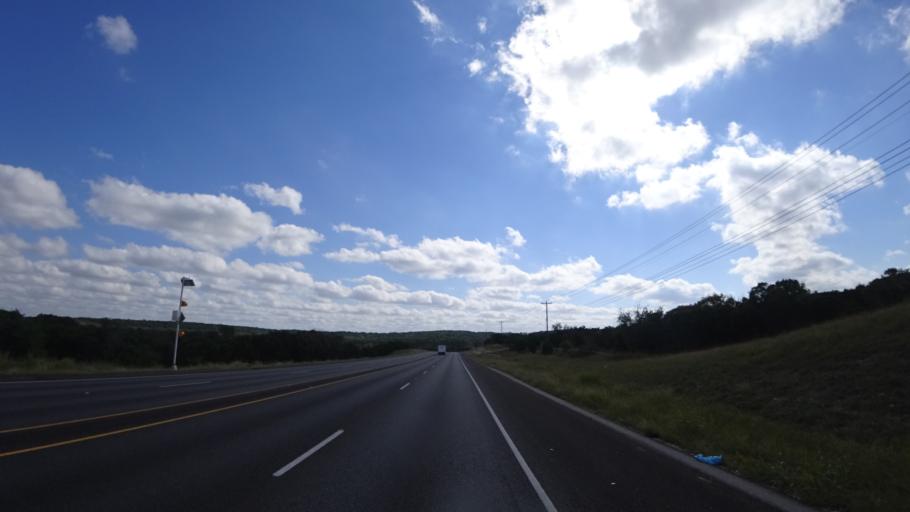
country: US
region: Texas
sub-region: Travis County
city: Barton Creek
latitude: 30.2714
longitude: -97.9122
